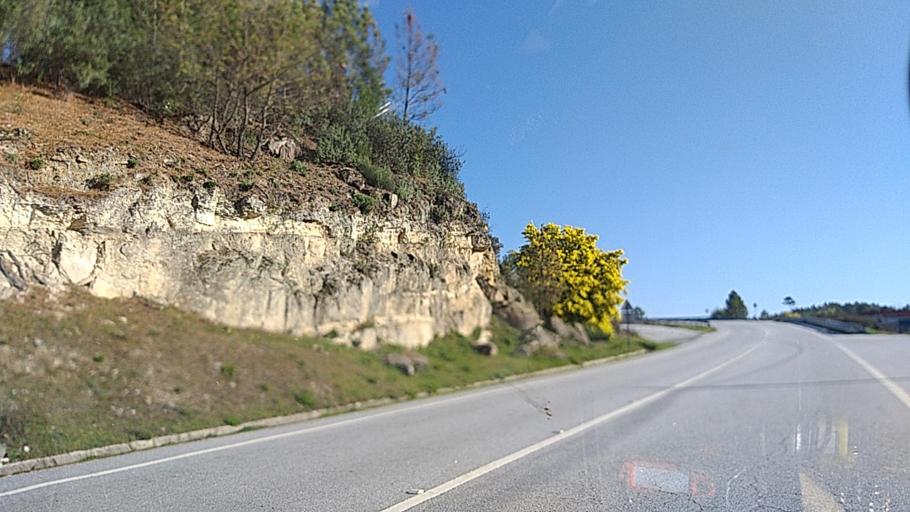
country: PT
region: Guarda
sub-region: Fornos de Algodres
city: Fornos de Algodres
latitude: 40.6173
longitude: -7.5135
